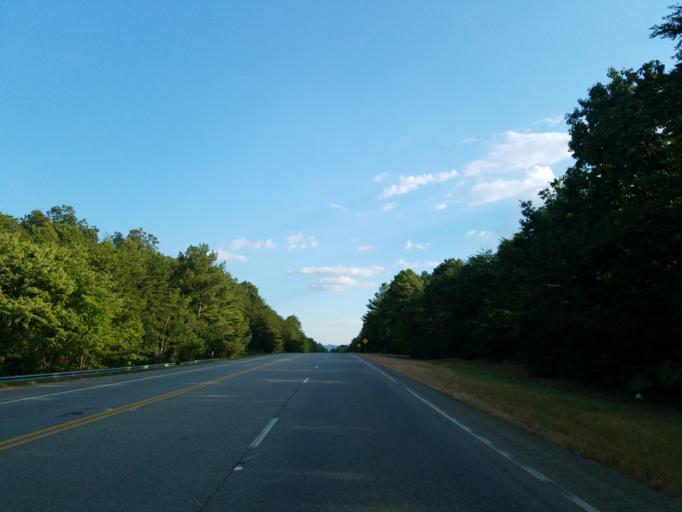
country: US
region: Georgia
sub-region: Murray County
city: Chatsworth
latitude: 34.6842
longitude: -84.7294
